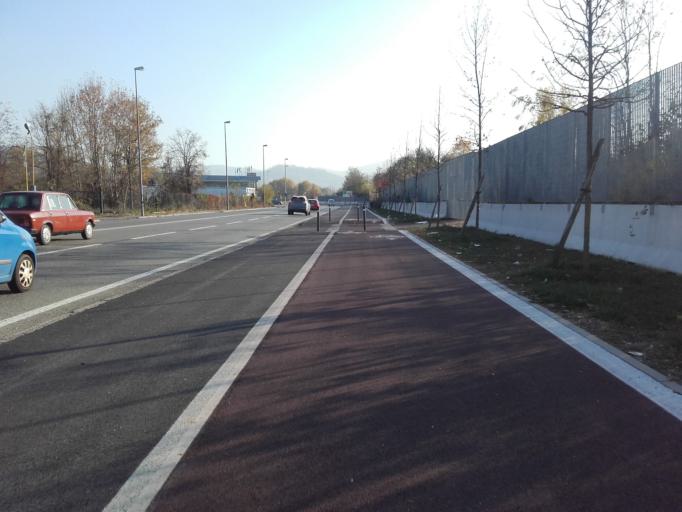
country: IT
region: Piedmont
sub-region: Provincia di Torino
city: Turin
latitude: 45.1016
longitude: 7.7210
